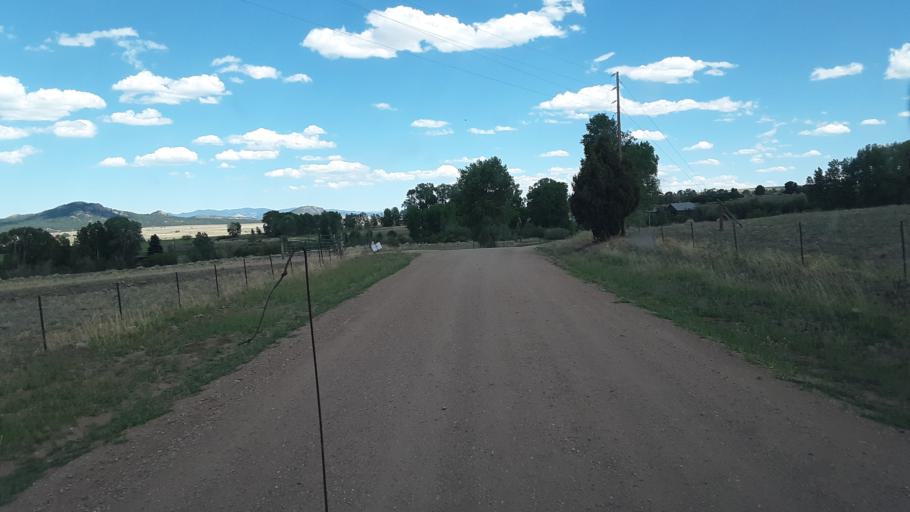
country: US
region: Colorado
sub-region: Custer County
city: Westcliffe
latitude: 38.2417
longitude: -105.6044
